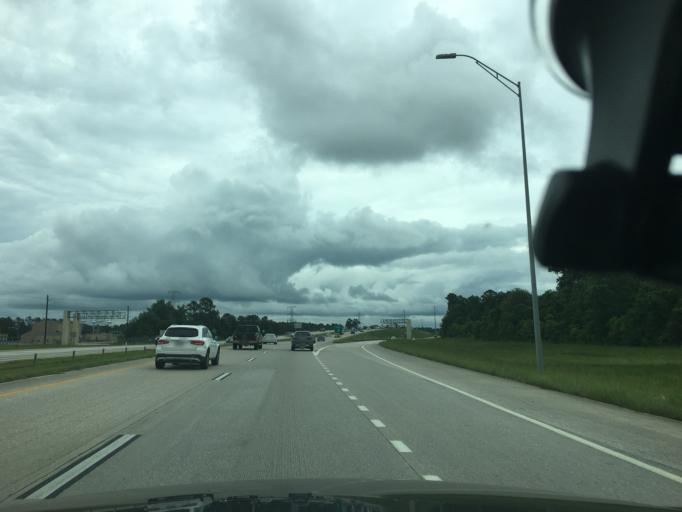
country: US
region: Texas
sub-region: Montgomery County
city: The Woodlands
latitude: 30.0938
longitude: -95.5126
